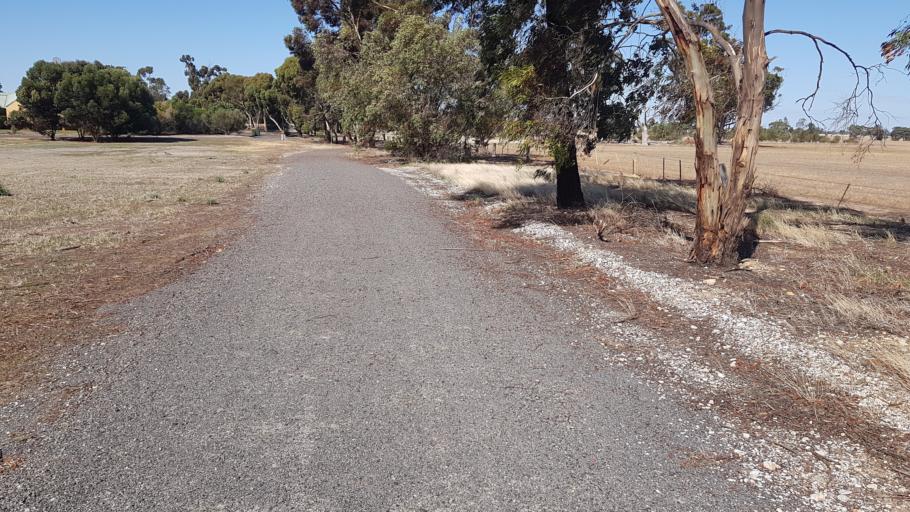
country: AU
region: Victoria
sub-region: Horsham
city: Horsham
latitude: -36.7465
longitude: 141.9361
